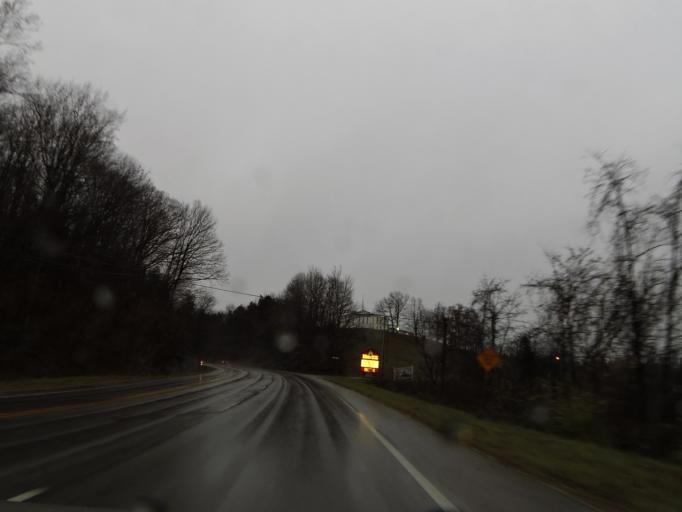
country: US
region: Kentucky
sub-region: Rockcastle County
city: Mount Vernon
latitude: 37.3492
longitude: -84.3326
